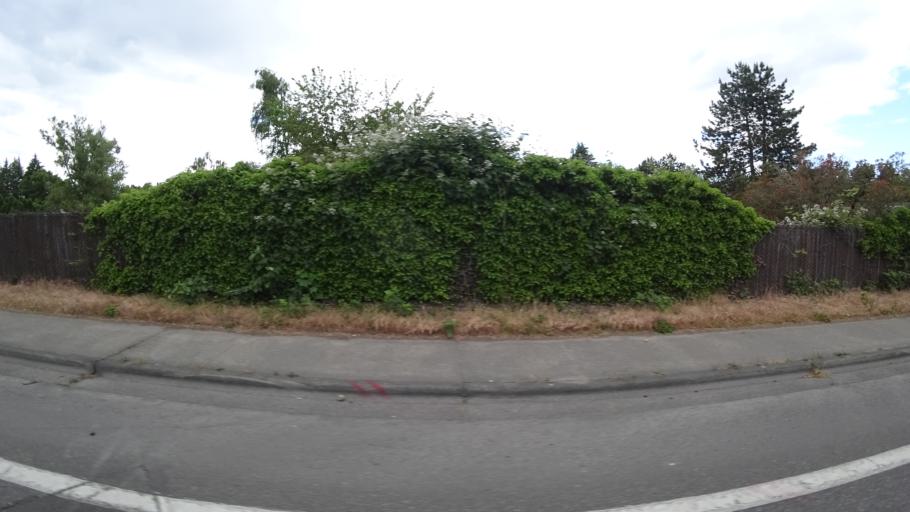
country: US
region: Oregon
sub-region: Washington County
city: Rockcreek
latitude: 45.5472
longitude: -122.8676
